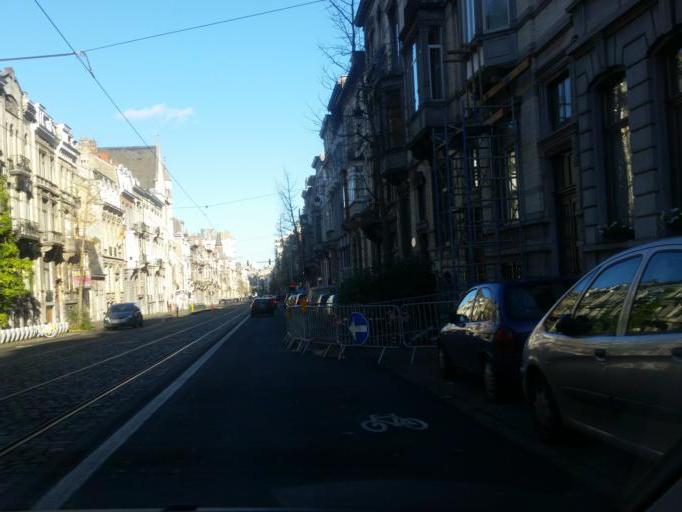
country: BE
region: Brussels Capital
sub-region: Bruxelles-Capitale
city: Brussels
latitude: 50.8174
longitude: 4.3504
